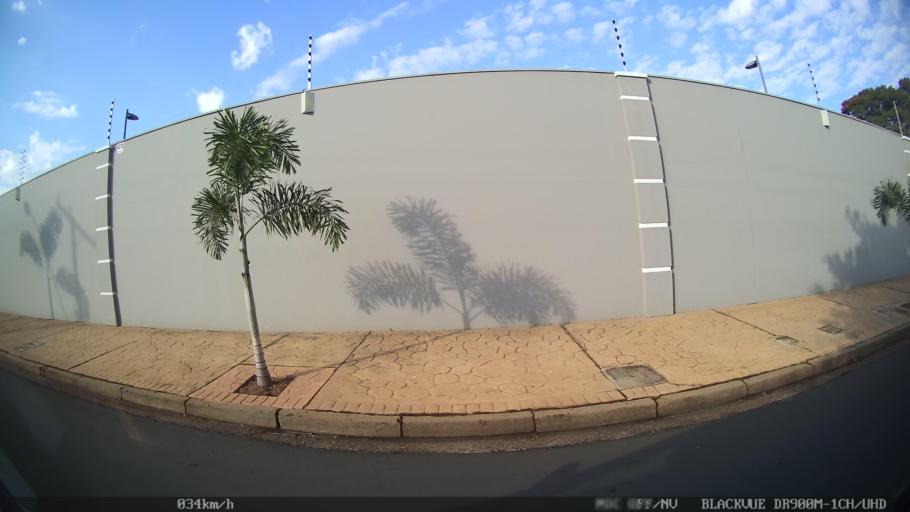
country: BR
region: Sao Paulo
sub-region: Americana
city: Americana
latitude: -22.7496
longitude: -47.3468
